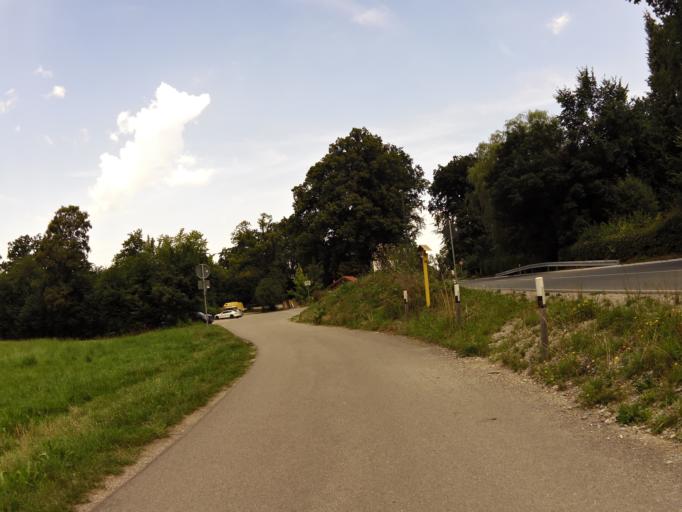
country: DE
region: Bavaria
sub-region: Upper Bavaria
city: Andechs
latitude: 47.9460
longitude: 11.1512
